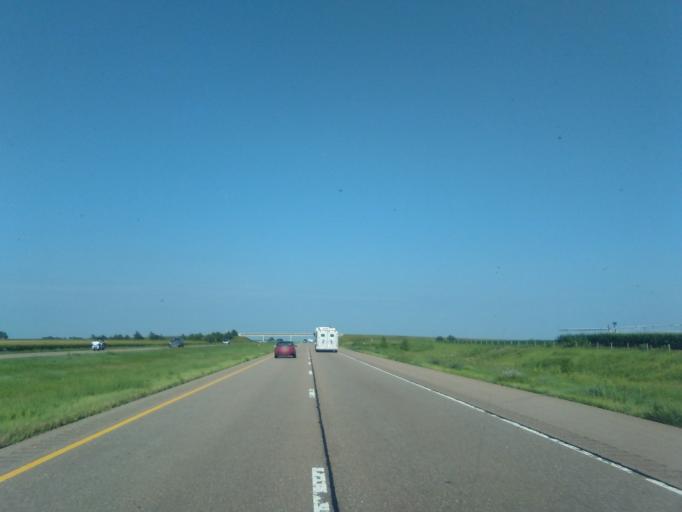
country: US
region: Nebraska
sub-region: Hamilton County
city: Aurora
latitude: 40.8220
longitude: -98.1178
